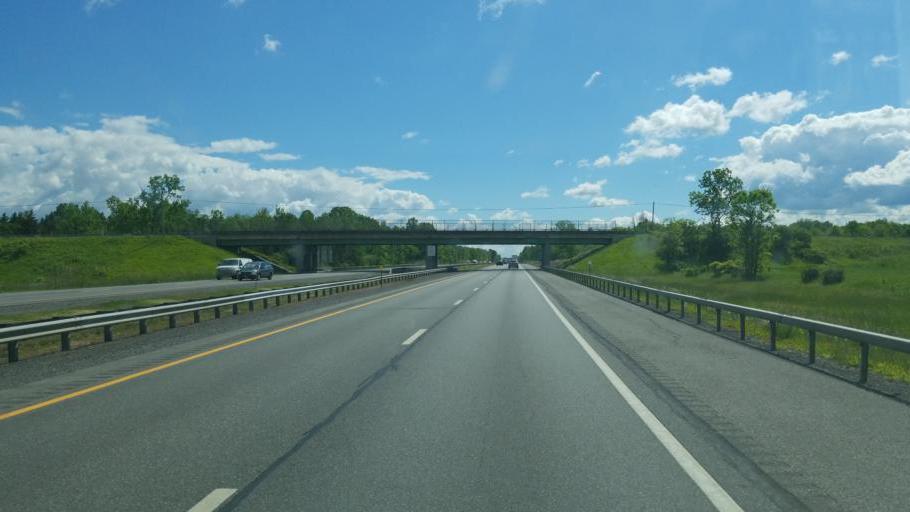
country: US
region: New York
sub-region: Madison County
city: Wampsville
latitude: 43.1016
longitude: -75.7239
